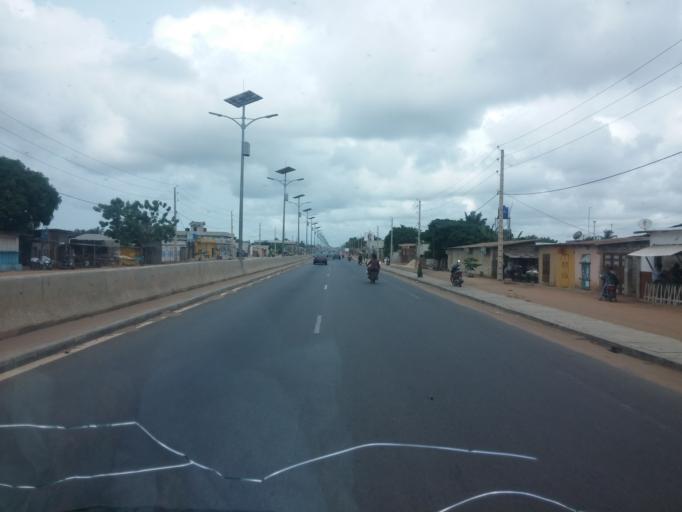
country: BJ
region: Atlantique
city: Hevie
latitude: 6.3866
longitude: 2.2253
